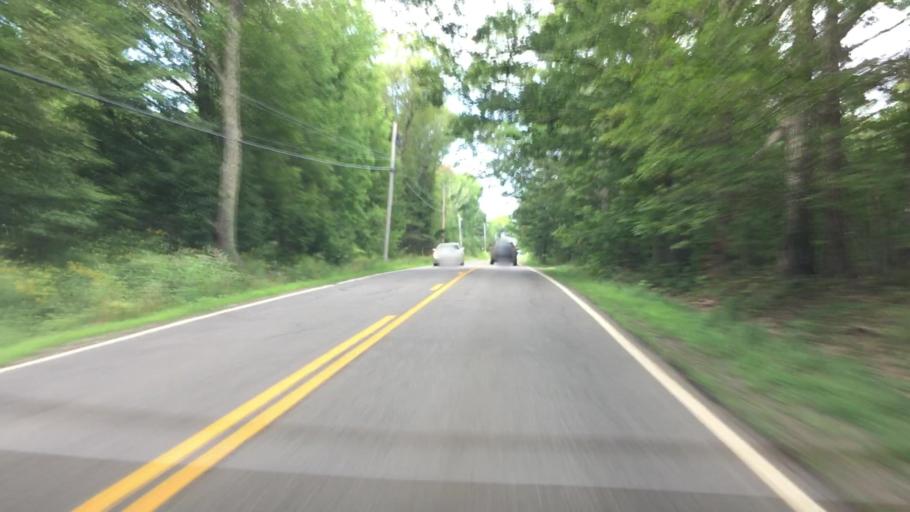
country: US
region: Maine
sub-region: Waldo County
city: Belfast
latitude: 44.3646
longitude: -69.0421
